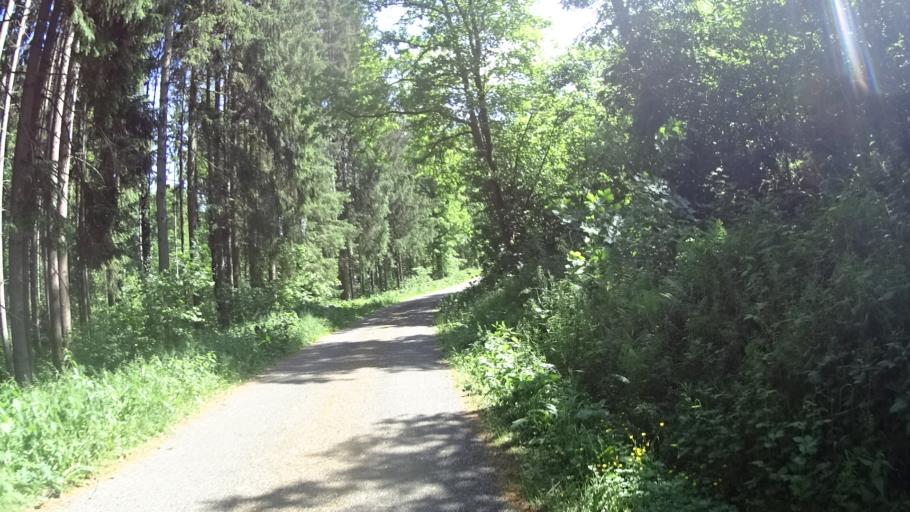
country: DE
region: Baden-Wuerttemberg
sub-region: Karlsruhe Region
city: Hopfingen
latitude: 49.6253
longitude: 9.4460
